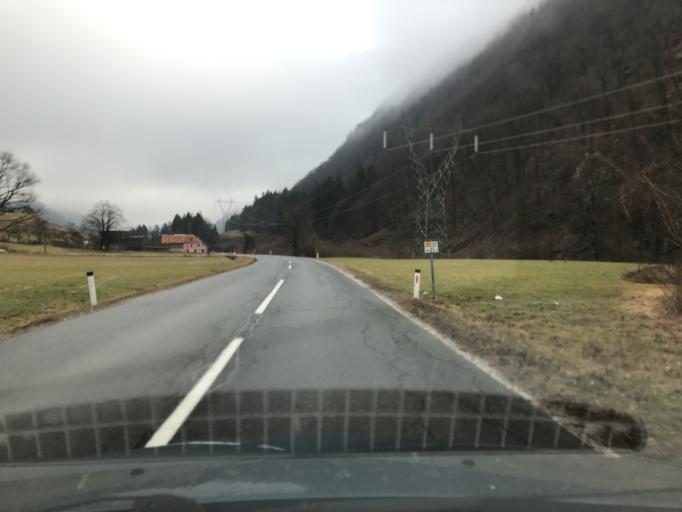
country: SI
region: Vransko
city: Vransko
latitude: 46.2141
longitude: 14.8641
